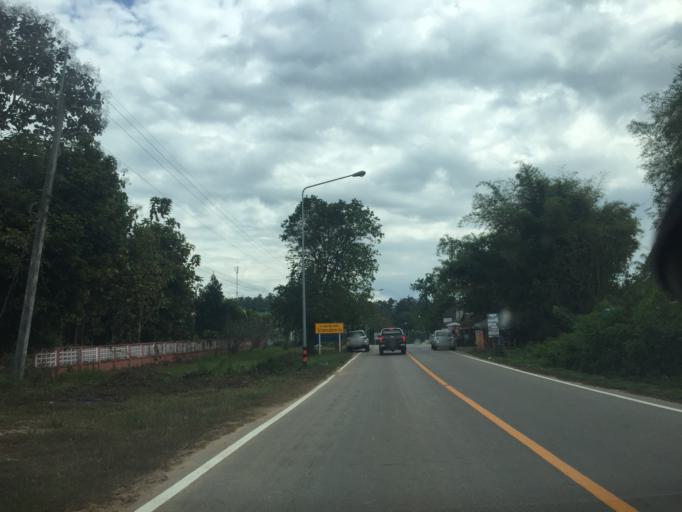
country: TH
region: Lampang
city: Mueang Pan
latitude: 18.8217
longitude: 99.5041
